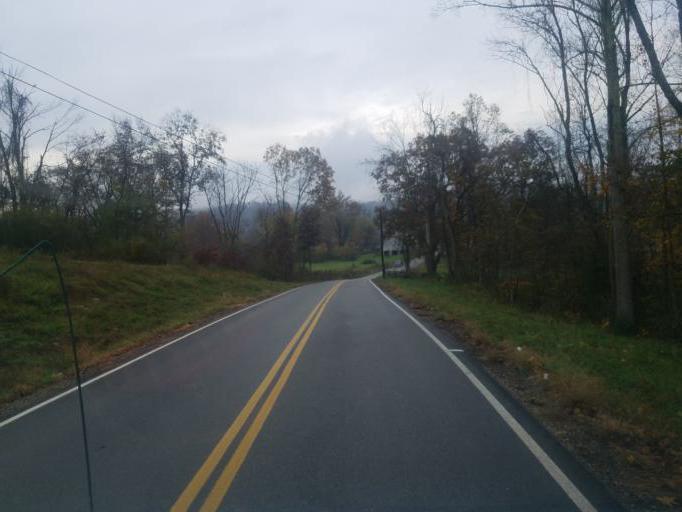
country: US
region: Ohio
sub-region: Morgan County
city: McConnelsville
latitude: 39.5649
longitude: -81.7843
